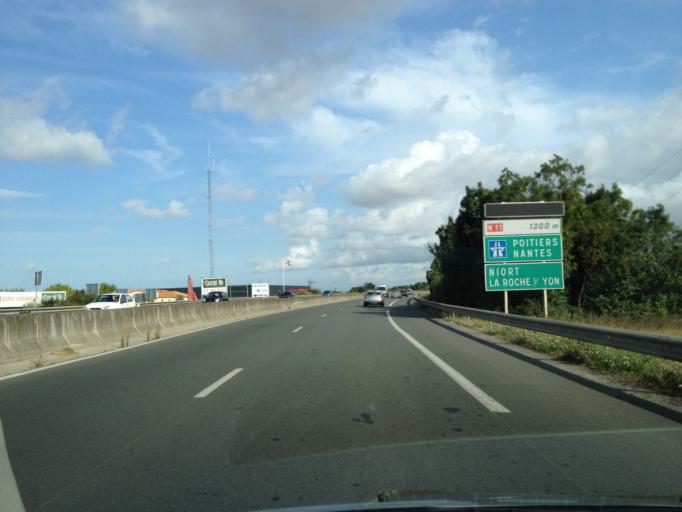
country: FR
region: Poitou-Charentes
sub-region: Departement de la Charente-Maritime
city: Perigny
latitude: 46.1586
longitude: -1.1194
